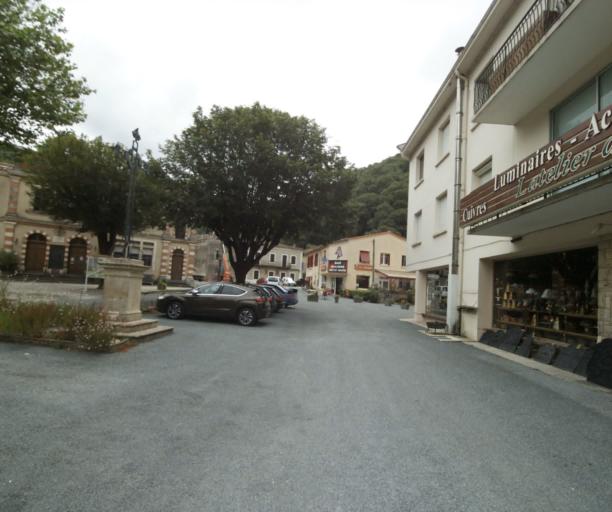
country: FR
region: Midi-Pyrenees
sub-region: Departement du Tarn
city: Soreze
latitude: 43.4387
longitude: 2.0663
